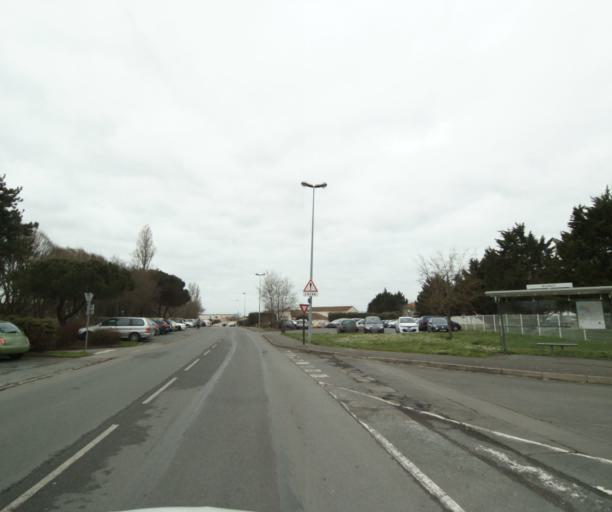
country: FR
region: Poitou-Charentes
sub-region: Departement de la Charente-Maritime
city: Lagord
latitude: 46.1786
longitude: -1.1481
